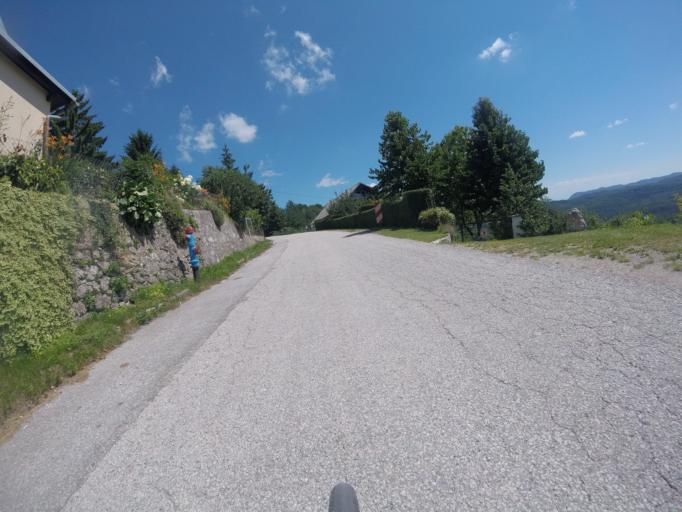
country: SI
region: Kostanjevica na Krki
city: Kostanjevica na Krki
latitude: 45.7731
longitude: 15.4699
